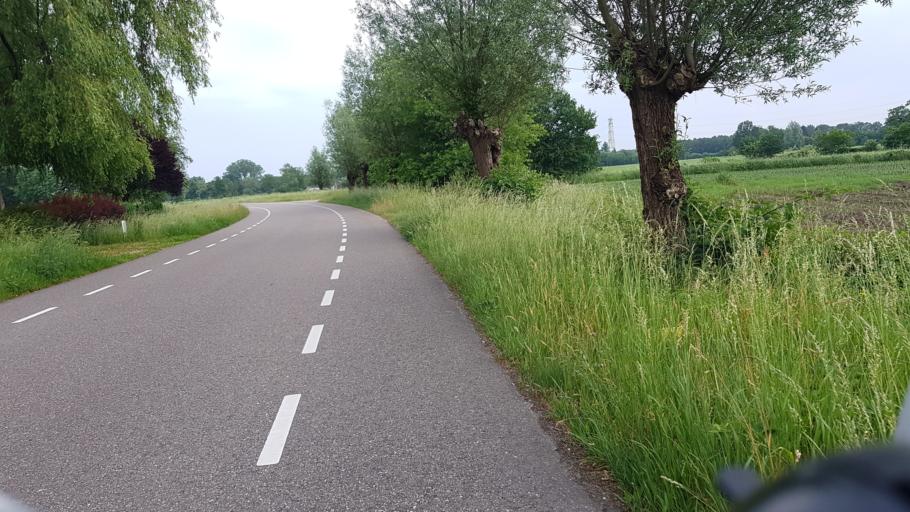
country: NL
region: Gelderland
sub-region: Gemeente Apeldoorn
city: Apeldoorn
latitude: 52.1968
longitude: 6.0221
